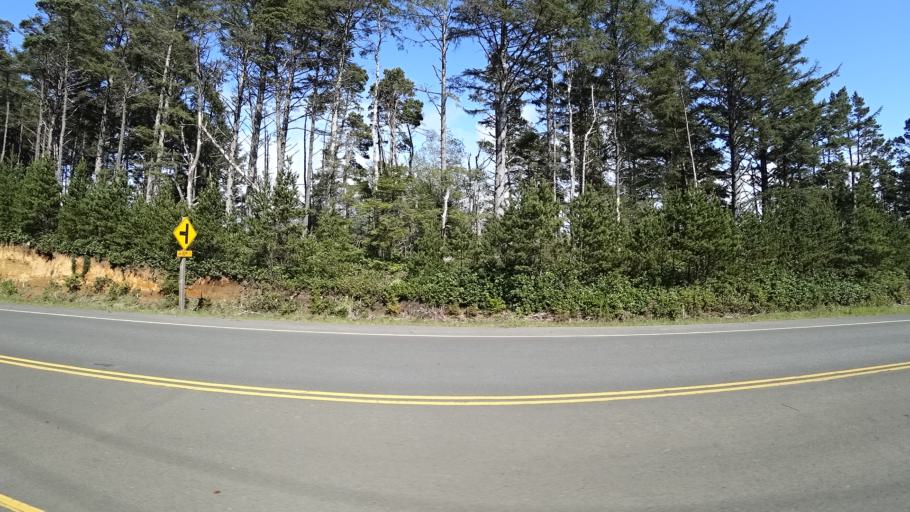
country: US
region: Oregon
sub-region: Lincoln County
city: Newport
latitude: 44.5776
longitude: -124.0659
